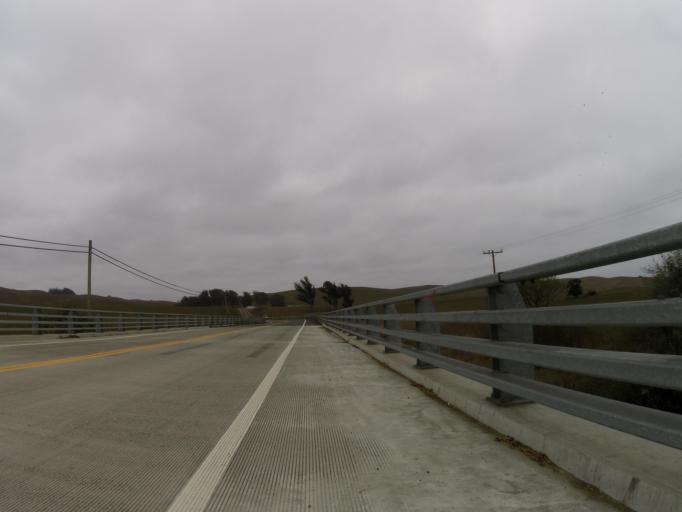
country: US
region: California
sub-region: Sonoma County
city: Occidental
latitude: 38.3133
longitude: -122.8973
